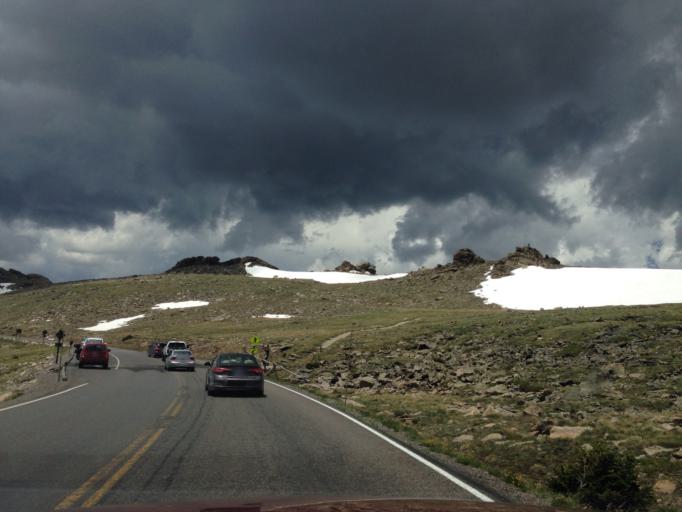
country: US
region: Colorado
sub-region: Larimer County
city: Estes Park
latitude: 40.4118
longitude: -105.7240
